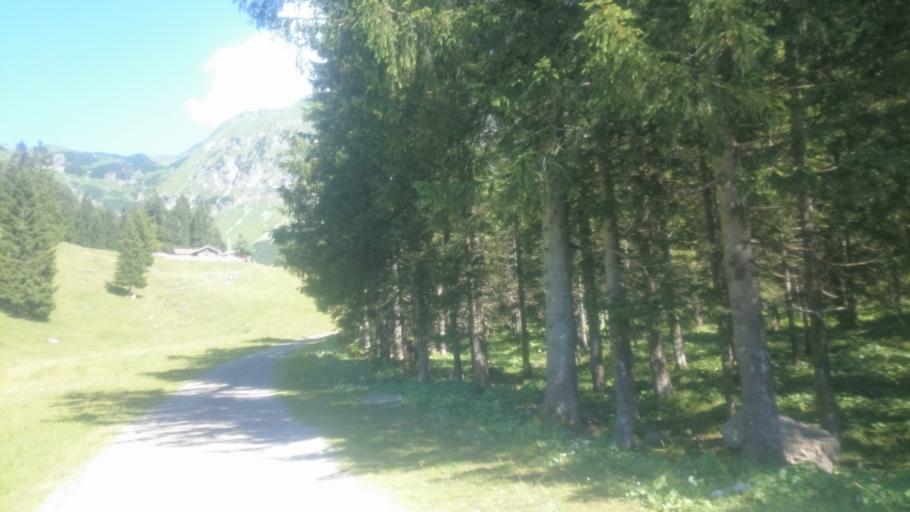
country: DE
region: Bavaria
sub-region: Swabia
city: Oberstdorf
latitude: 47.4088
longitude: 10.3210
